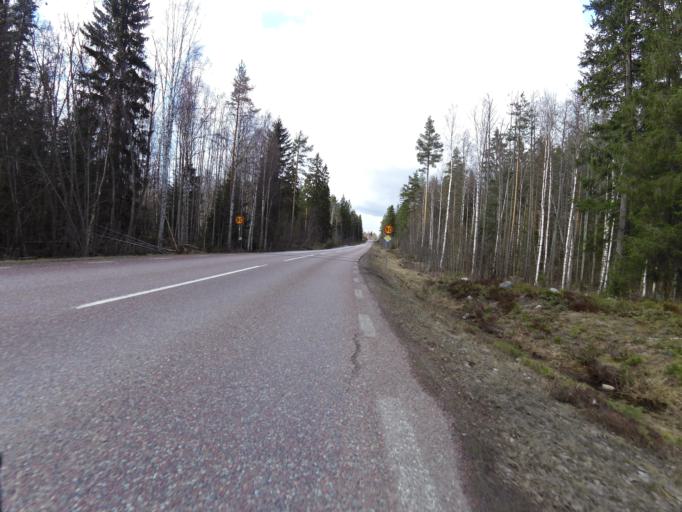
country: SE
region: Gaevleborg
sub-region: Hofors Kommun
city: Hofors
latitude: 60.5005
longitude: 16.4297
